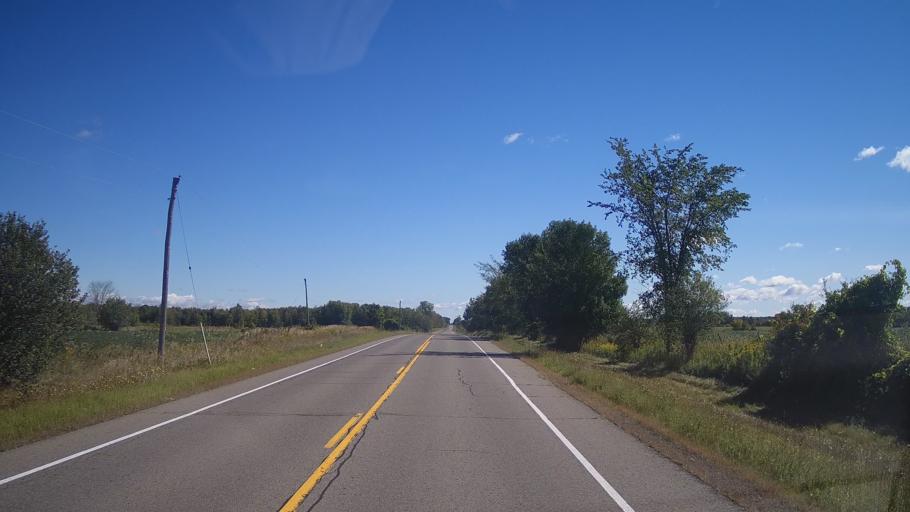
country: CA
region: Ontario
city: Prescott
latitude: 44.9285
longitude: -75.3360
